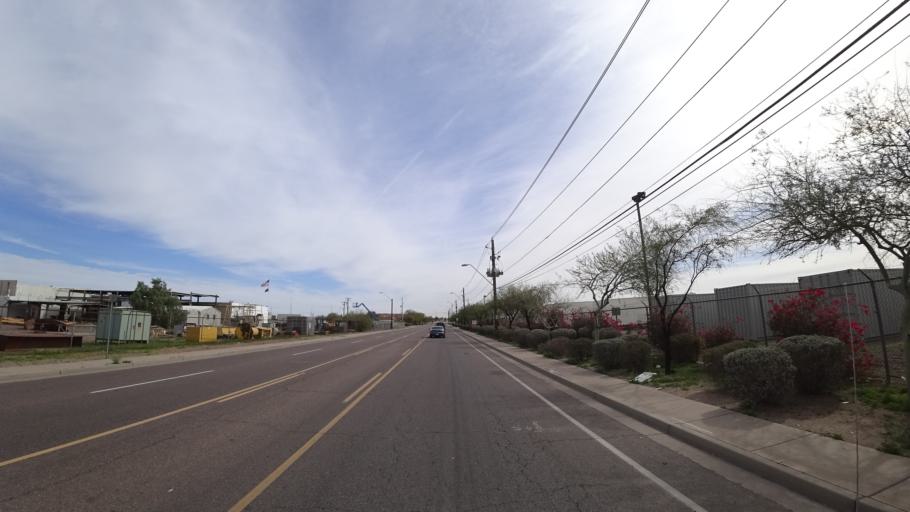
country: US
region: Arizona
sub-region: Maricopa County
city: Phoenix
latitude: 33.4295
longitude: -112.1128
